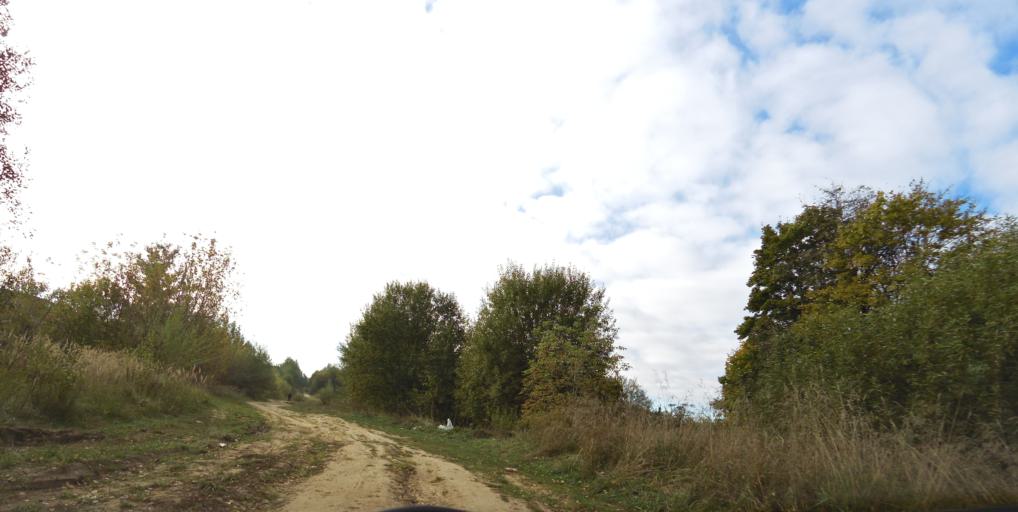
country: LT
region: Vilnius County
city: Justiniskes
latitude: 54.7191
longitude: 25.2103
